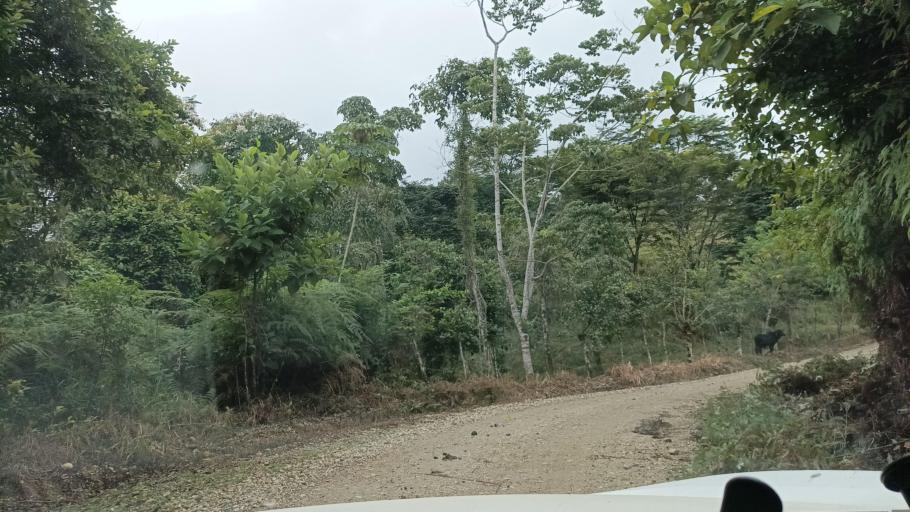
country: MX
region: Veracruz
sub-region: Uxpanapa
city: Poblado 10
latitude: 17.4332
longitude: -94.4164
